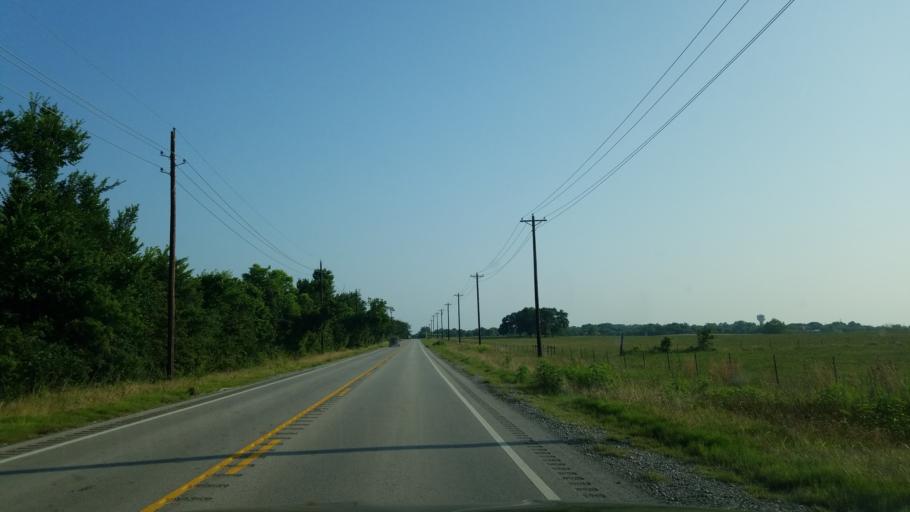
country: US
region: Texas
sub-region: Denton County
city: Aubrey
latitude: 33.3168
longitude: -96.9767
